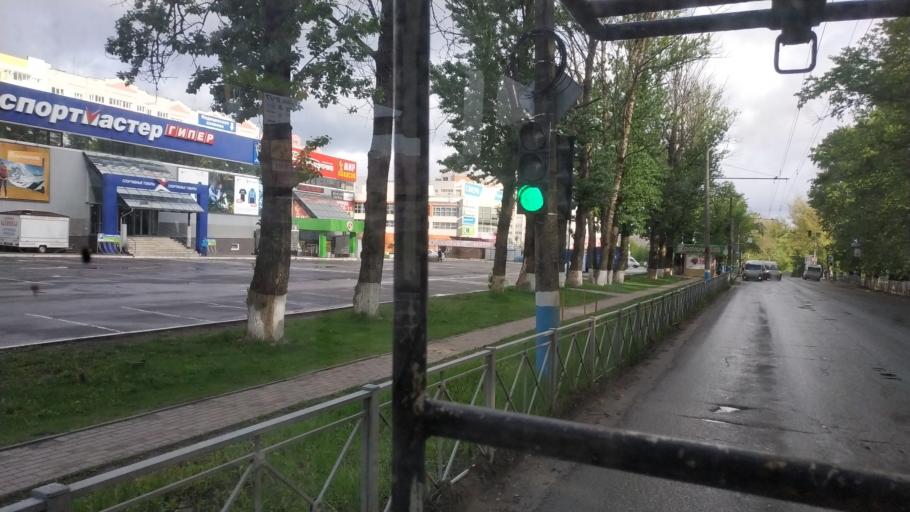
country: RU
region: Brjansk
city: Putevka
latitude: 53.2637
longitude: 34.3238
